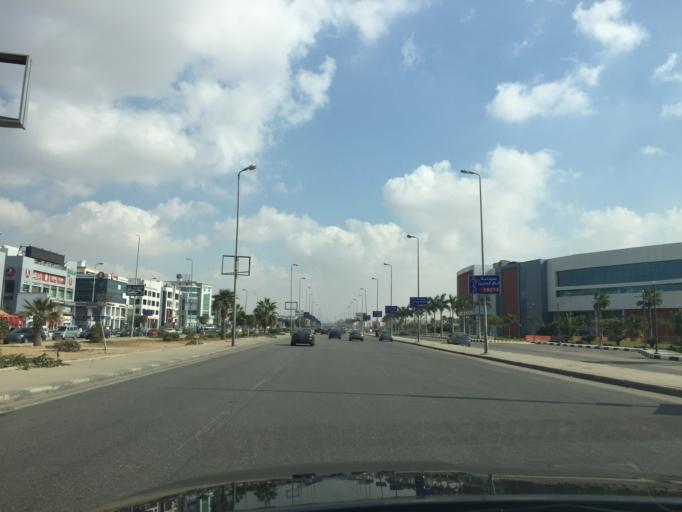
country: EG
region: Muhafazat al Qalyubiyah
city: Al Khankah
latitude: 30.0254
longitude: 31.4634
